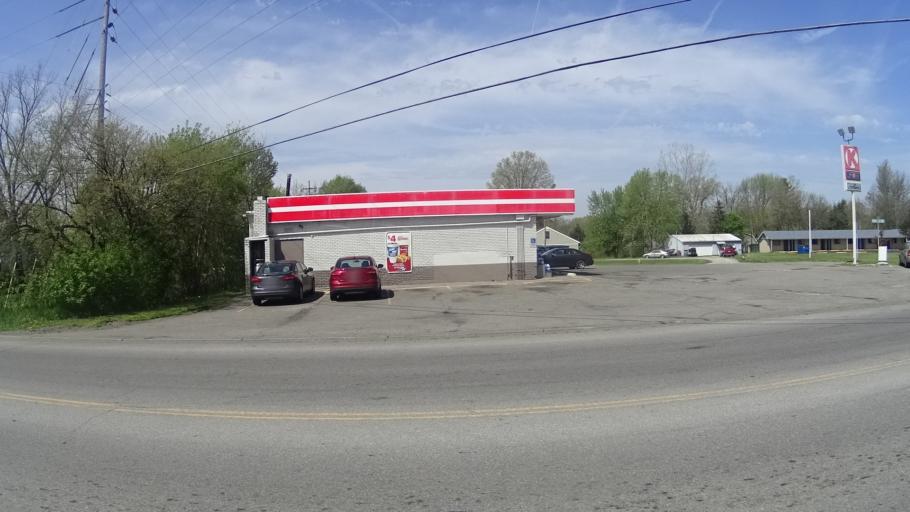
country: US
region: Ohio
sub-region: Lorain County
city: Elyria
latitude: 41.3373
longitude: -82.1175
